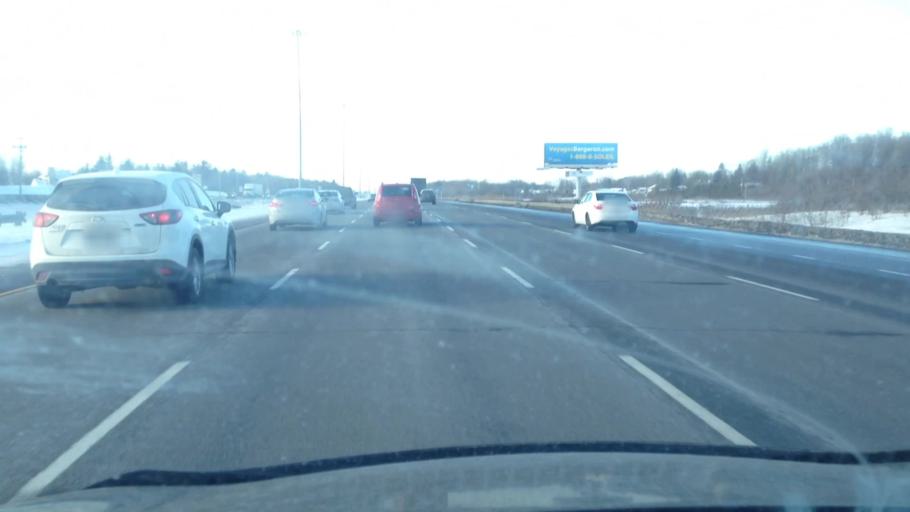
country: CA
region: Quebec
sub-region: Laurentides
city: Blainville
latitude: 45.6480
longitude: -73.8702
